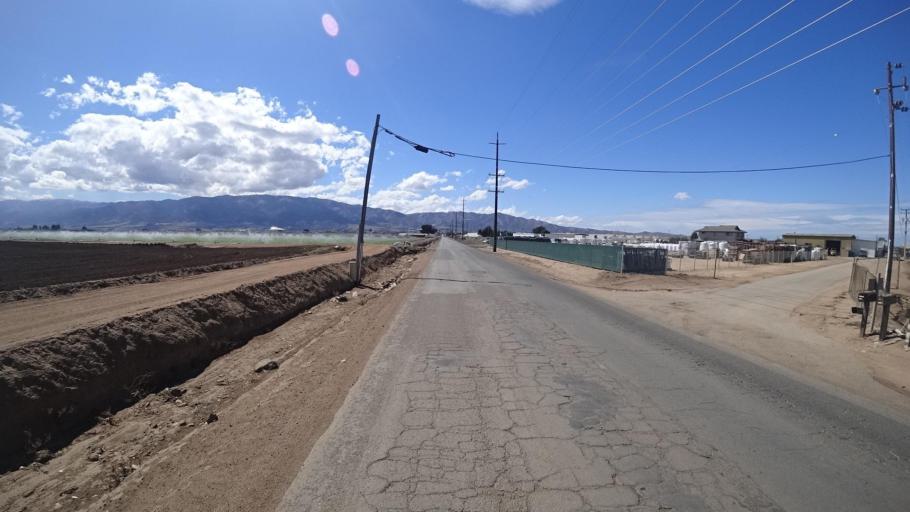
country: US
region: California
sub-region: Monterey County
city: Chualar
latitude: 36.6208
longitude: -121.5558
